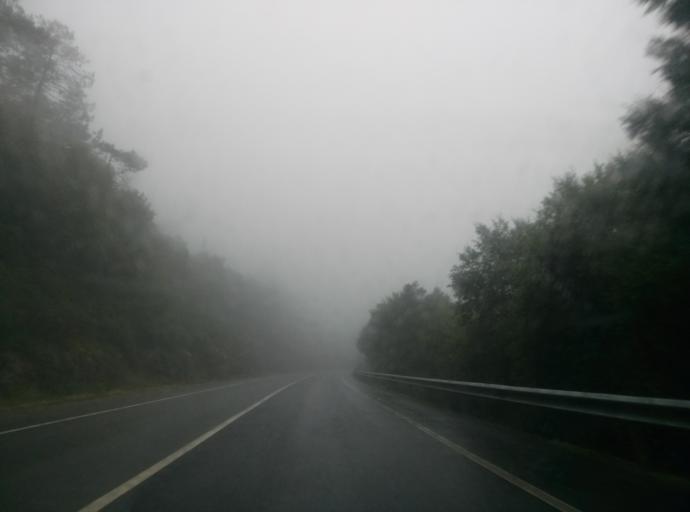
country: ES
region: Galicia
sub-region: Provincia de Lugo
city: Muras
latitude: 43.5202
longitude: -7.6708
